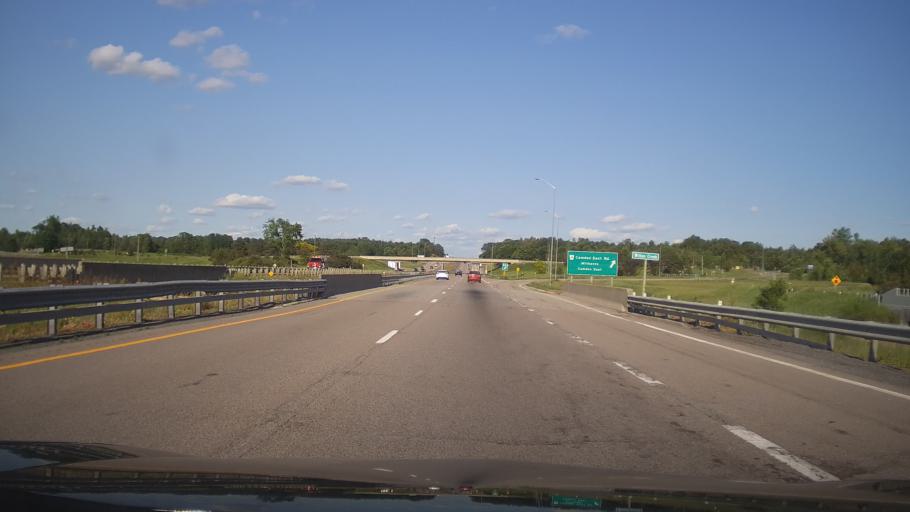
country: CA
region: Ontario
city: Skatepark
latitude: 44.2790
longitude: -76.7903
